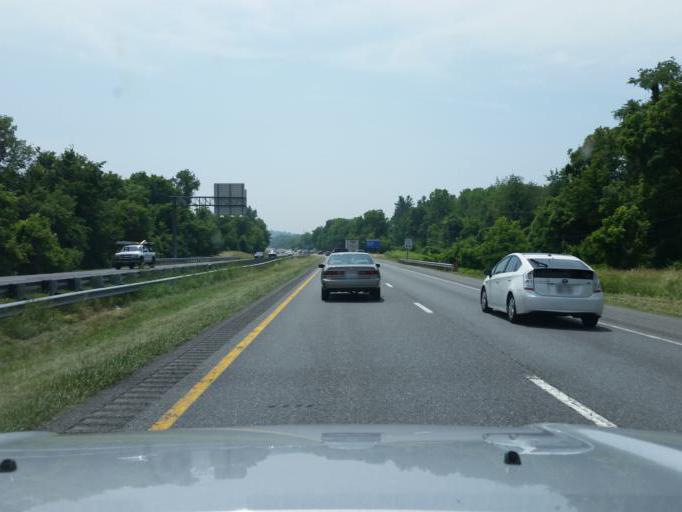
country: US
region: Maryland
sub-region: Frederick County
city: Ballenger Creek
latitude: 39.3749
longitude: -77.4054
